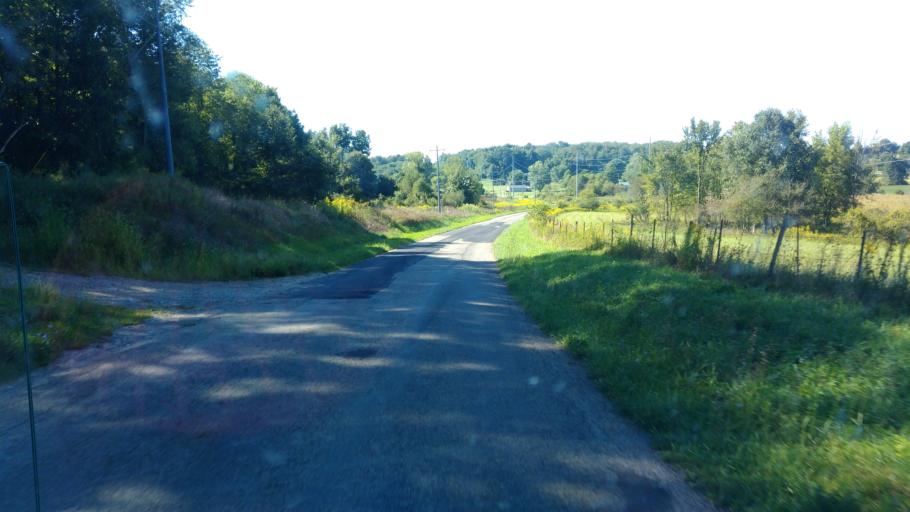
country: US
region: Ohio
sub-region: Knox County
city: Fredericktown
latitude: 40.4779
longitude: -82.4602
